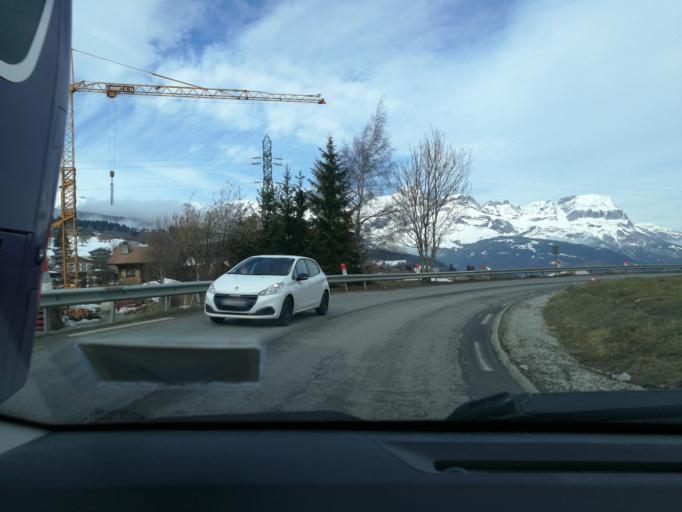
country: FR
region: Rhone-Alpes
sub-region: Departement de la Haute-Savoie
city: Combloux
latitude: 45.8880
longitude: 6.6492
